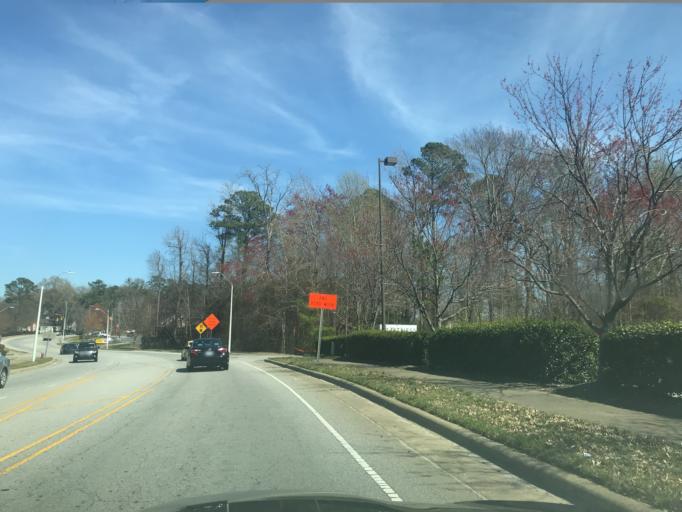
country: US
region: North Carolina
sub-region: Wake County
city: Fuquay-Varina
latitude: 35.5941
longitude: -78.7769
